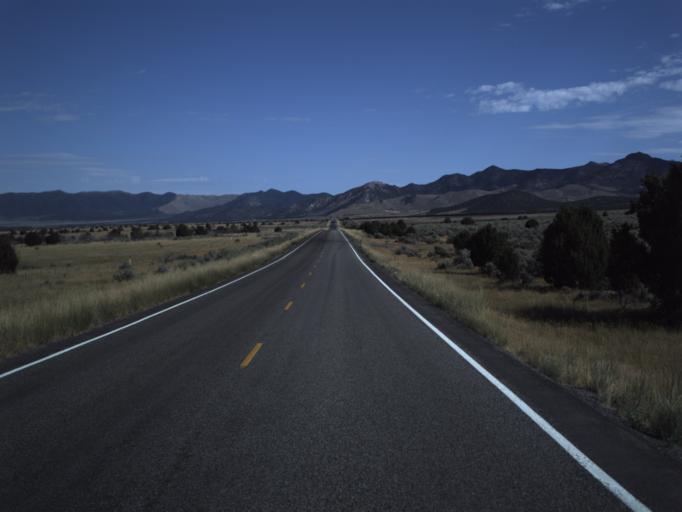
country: US
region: Utah
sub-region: Juab County
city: Mona
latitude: 39.8534
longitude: -112.1381
